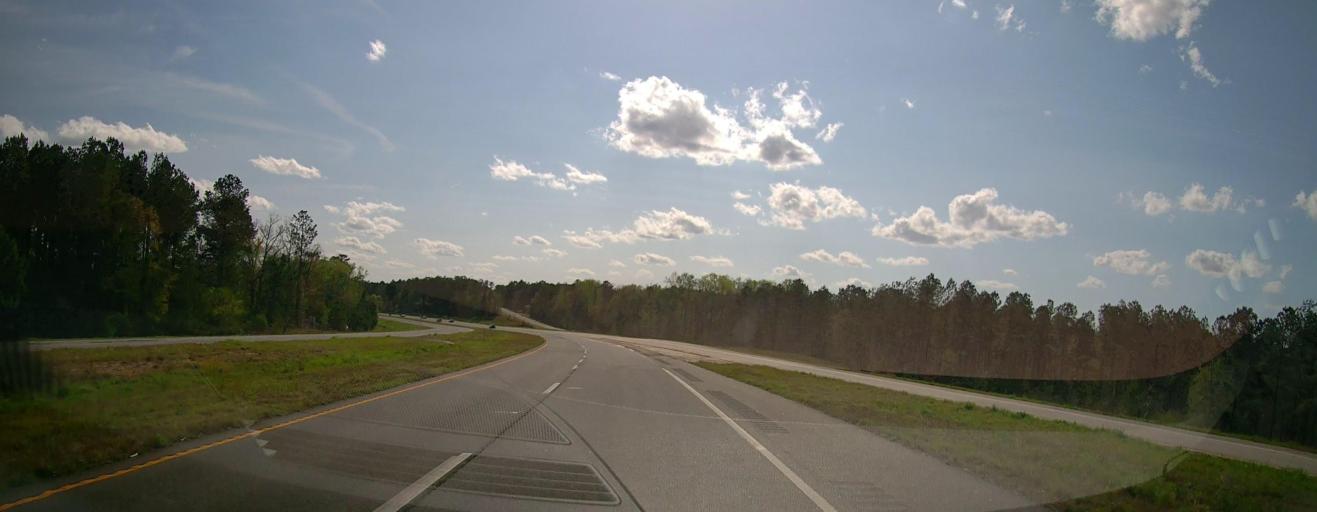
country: US
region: Georgia
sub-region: Baldwin County
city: Hardwick
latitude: 32.9781
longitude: -83.2194
